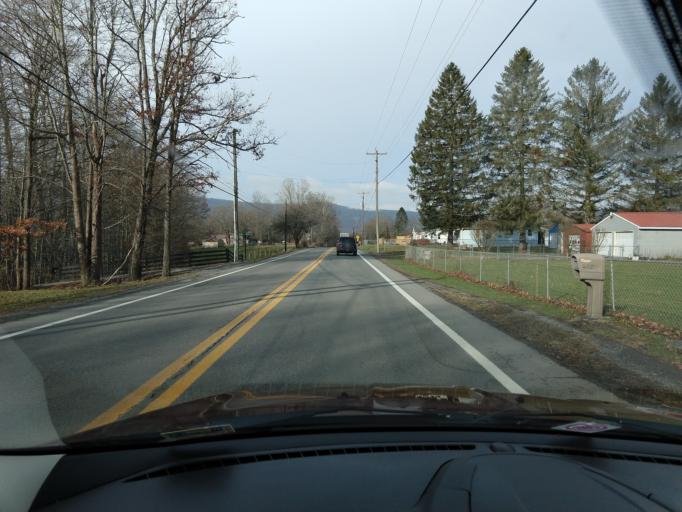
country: US
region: West Virginia
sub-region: Greenbrier County
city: Rainelle
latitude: 37.9534
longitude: -80.6746
